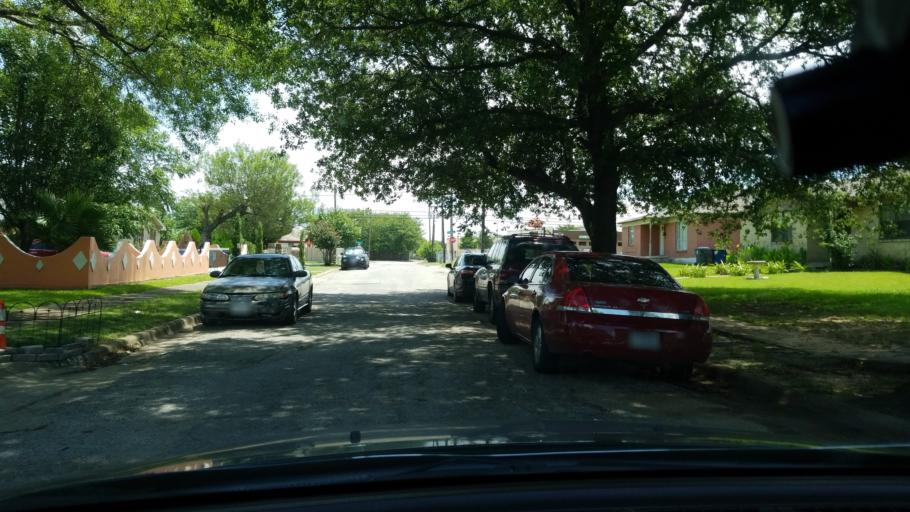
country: US
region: Texas
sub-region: Dallas County
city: Balch Springs
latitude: 32.7365
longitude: -96.6492
